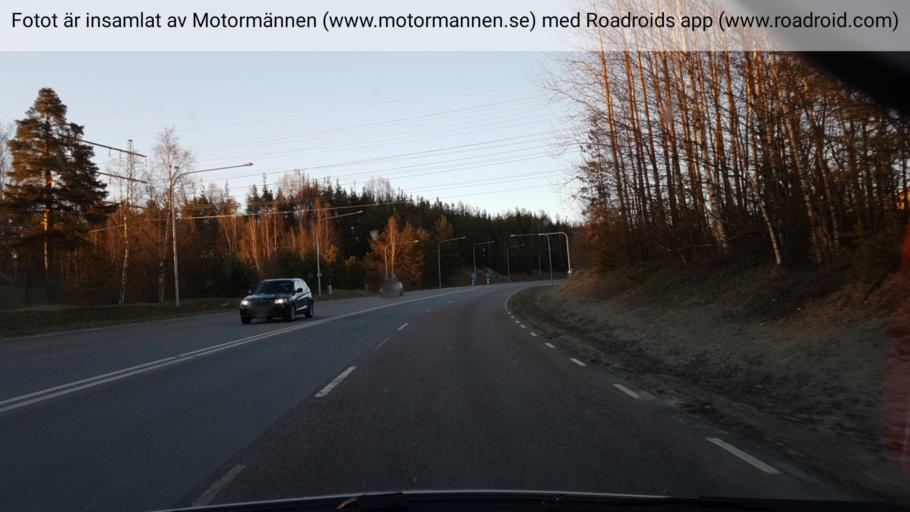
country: SE
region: Vaesternorrland
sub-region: OErnskoeldsviks Kommun
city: Ornskoldsvik
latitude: 63.2735
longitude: 18.6936
